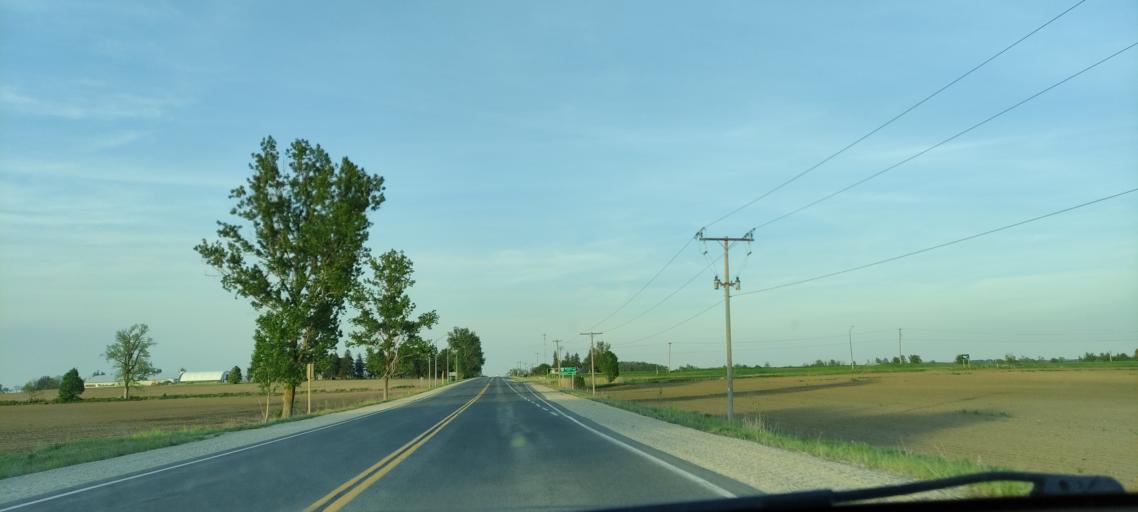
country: CA
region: Ontario
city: London
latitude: 43.2210
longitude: -81.1660
